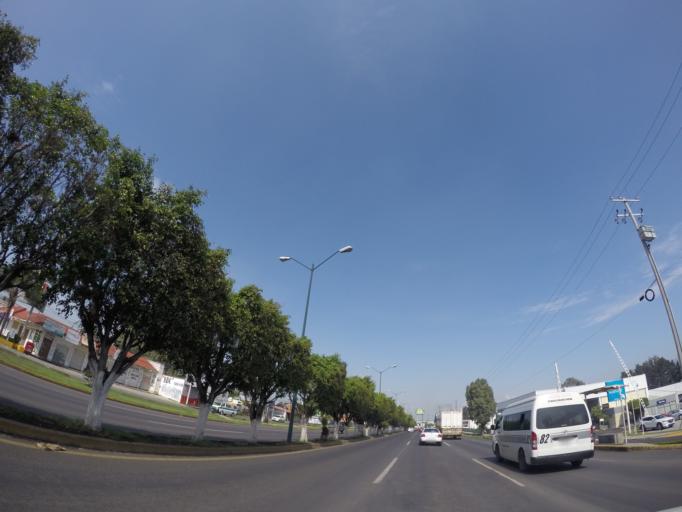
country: MX
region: Michoacan
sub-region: Morelia
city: Morelos
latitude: 19.6769
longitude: -101.2265
